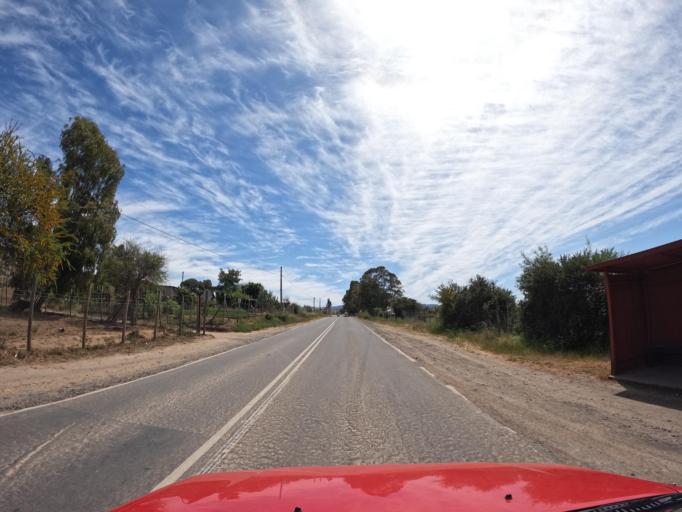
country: CL
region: Maule
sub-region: Provincia de Talca
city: Talca
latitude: -35.1221
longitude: -71.6747
